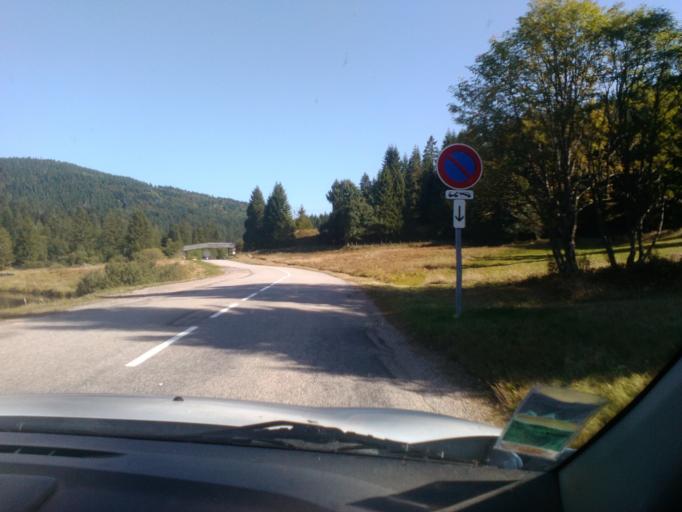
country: FR
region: Lorraine
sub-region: Departement des Vosges
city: Xonrupt-Longemer
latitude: 48.0404
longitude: 6.9312
